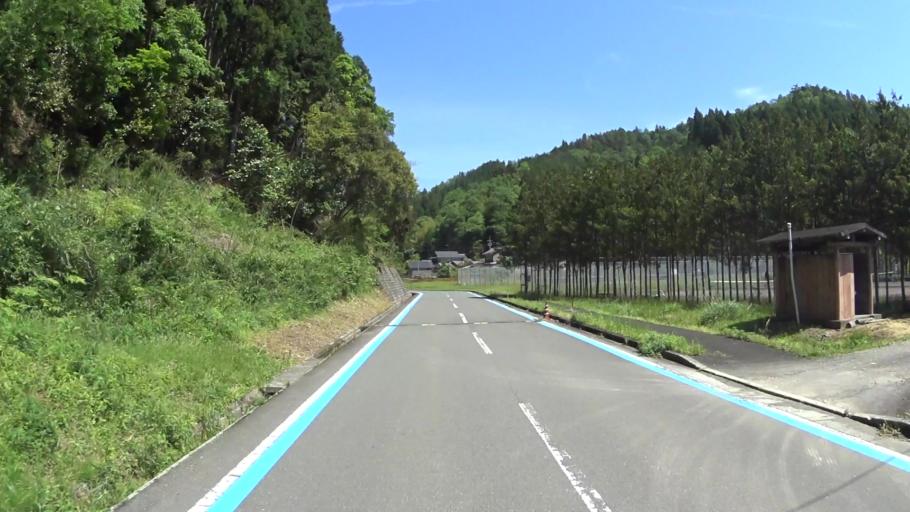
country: JP
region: Kyoto
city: Maizuru
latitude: 35.3725
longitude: 135.4375
